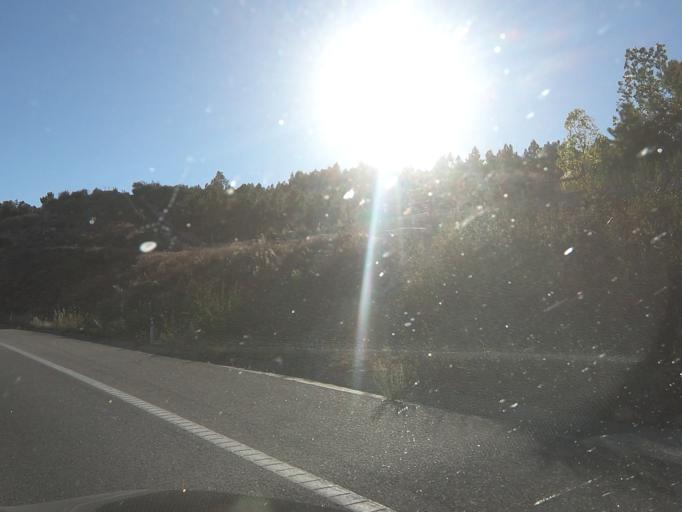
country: PT
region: Vila Real
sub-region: Murca
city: Murca
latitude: 41.3859
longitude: -7.4801
